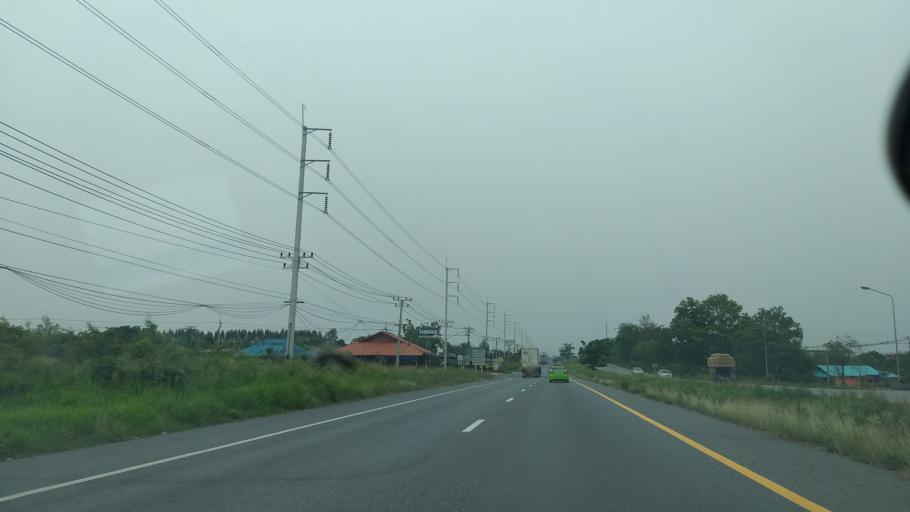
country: TH
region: Chon Buri
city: Ko Chan
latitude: 13.4320
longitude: 101.2829
